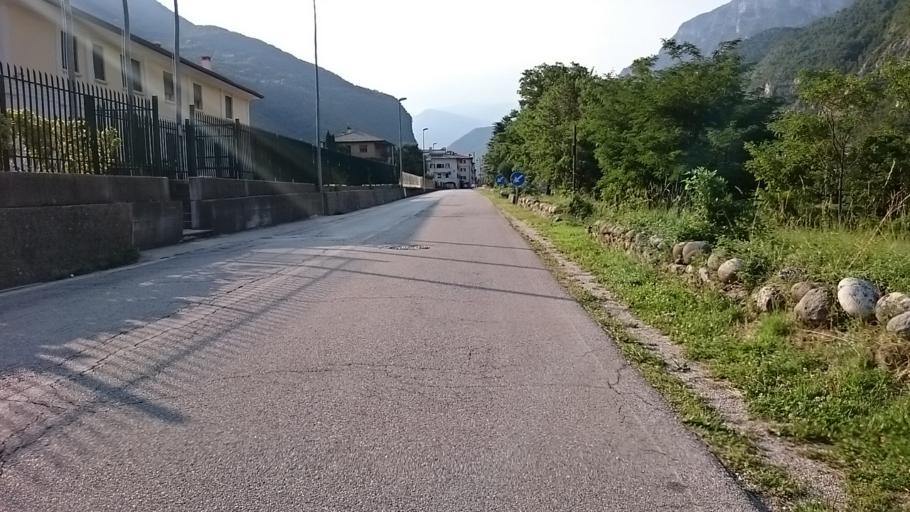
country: IT
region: Veneto
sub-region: Provincia di Vicenza
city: Campolongo sul Brenta
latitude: 45.8227
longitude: 11.7076
